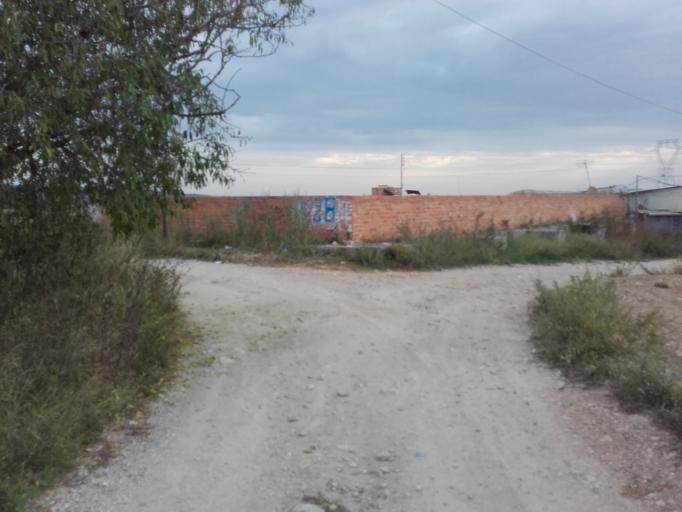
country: ES
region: Catalonia
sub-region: Provincia de Tarragona
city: Santa Oliva
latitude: 41.2496
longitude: 1.5469
